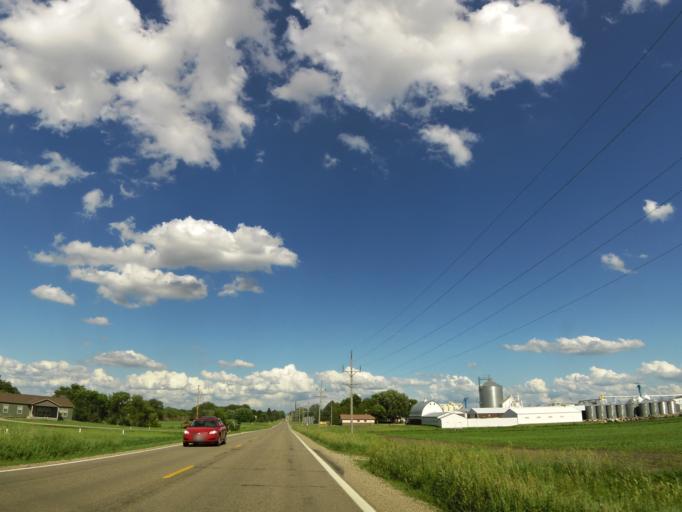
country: US
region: Minnesota
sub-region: Wright County
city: Cokato
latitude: 45.0657
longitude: -94.2062
